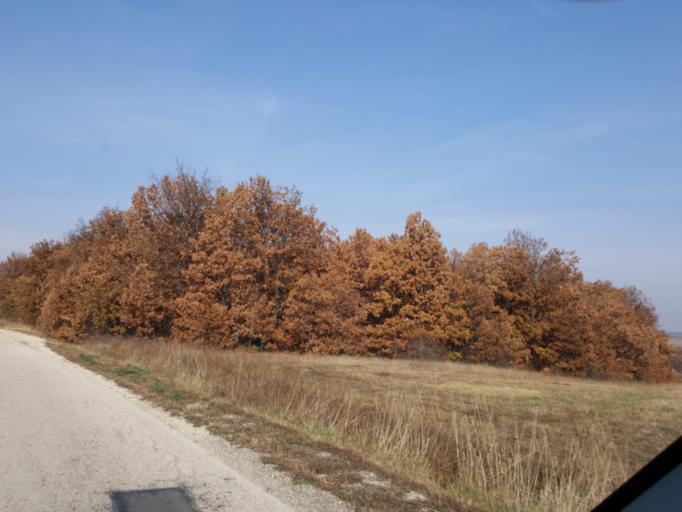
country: RS
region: Central Serbia
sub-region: Borski Okrug
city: Bor
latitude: 43.9922
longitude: 22.0728
